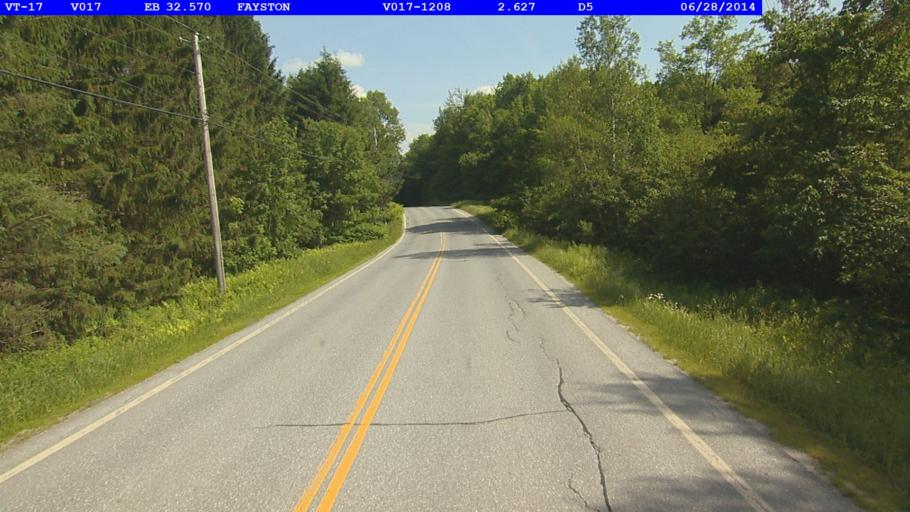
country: US
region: Vermont
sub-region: Washington County
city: Waterbury
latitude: 44.1999
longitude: -72.8949
